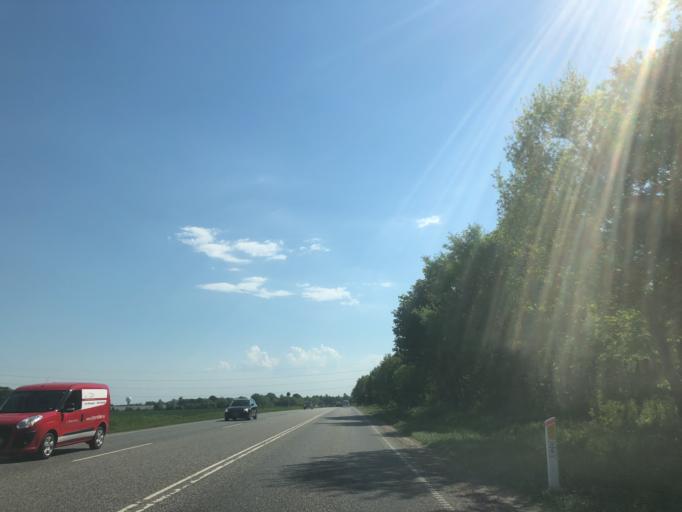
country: DK
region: Zealand
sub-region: Roskilde Kommune
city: Roskilde
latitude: 55.6057
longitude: 12.1009
